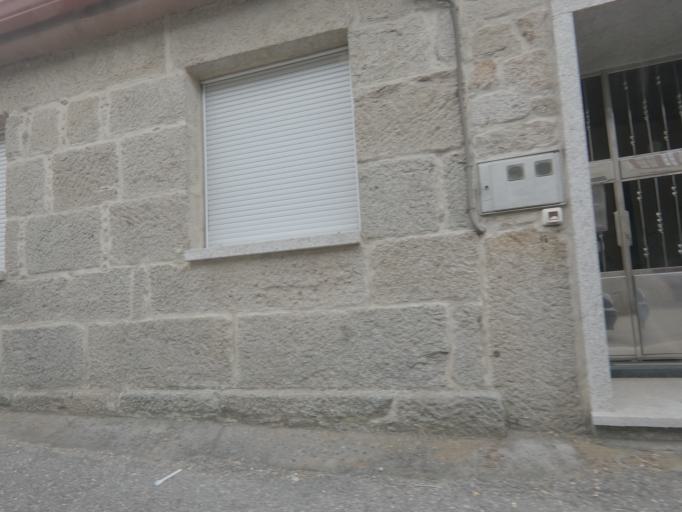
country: ES
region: Galicia
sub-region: Provincia de Pontevedra
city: Tui
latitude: 42.0495
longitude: -8.6587
